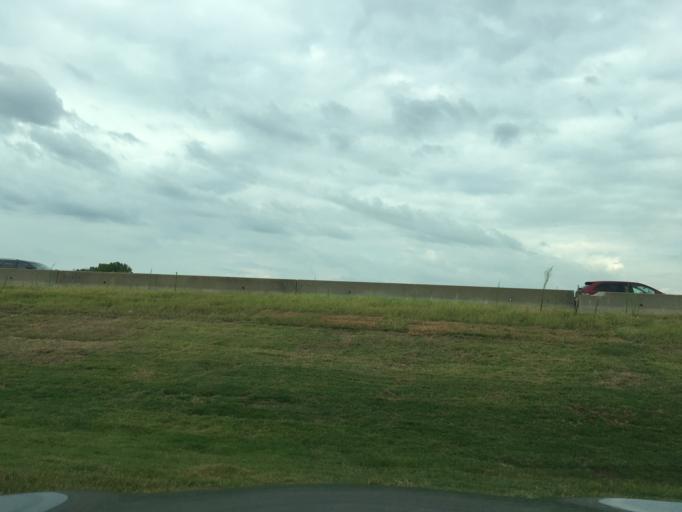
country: US
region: Texas
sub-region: Collin County
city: Melissa
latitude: 33.3255
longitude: -96.5896
